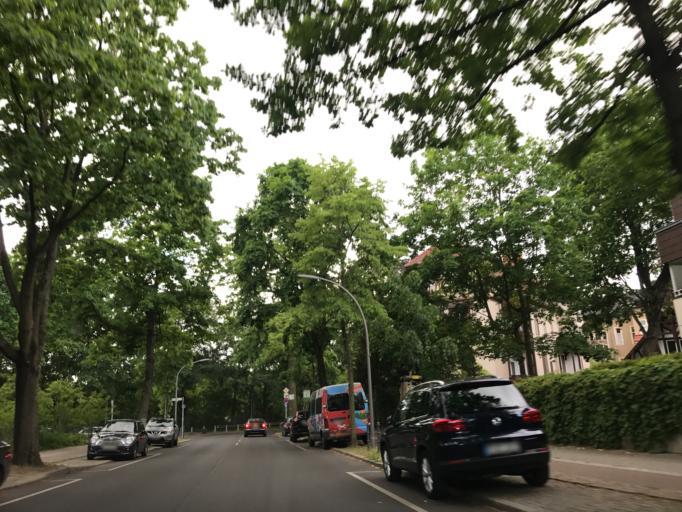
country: DE
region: Berlin
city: Halensee
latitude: 52.4871
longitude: 13.2861
